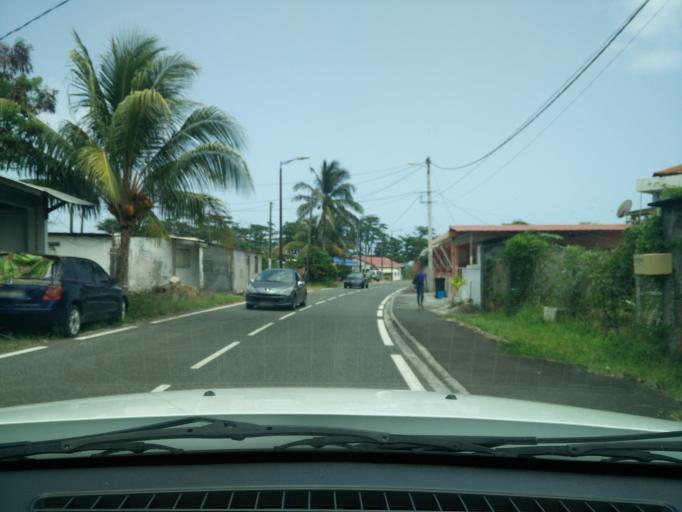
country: GP
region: Guadeloupe
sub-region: Guadeloupe
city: Capesterre-Belle-Eau
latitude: 16.0521
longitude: -61.5582
